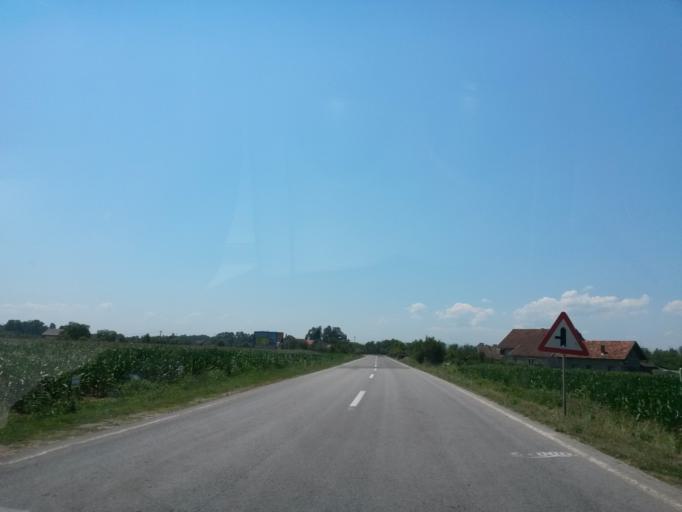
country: BA
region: Federation of Bosnia and Herzegovina
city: Odzak
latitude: 44.9956
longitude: 18.3847
